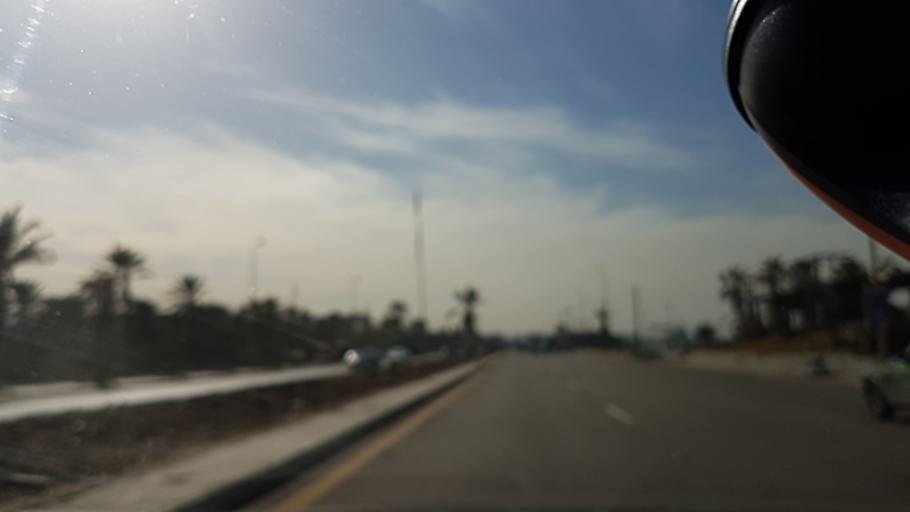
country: LB
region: Liban-Sud
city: Sidon
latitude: 33.5951
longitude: 35.3888
